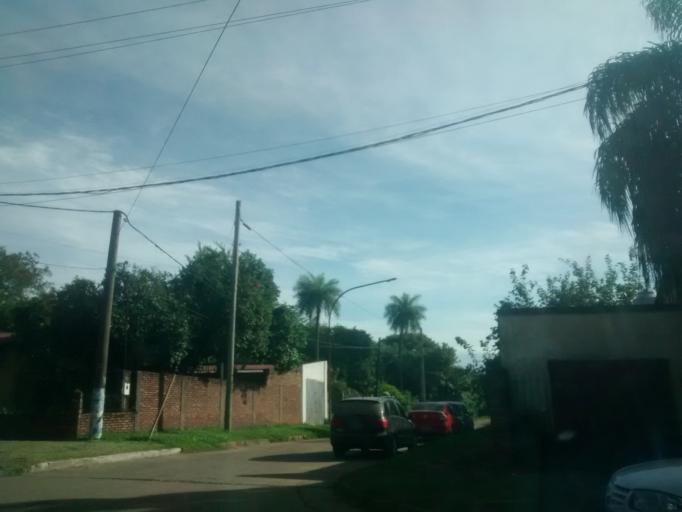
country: AR
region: Chaco
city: Puerto Tirol
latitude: -27.3721
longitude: -59.0893
